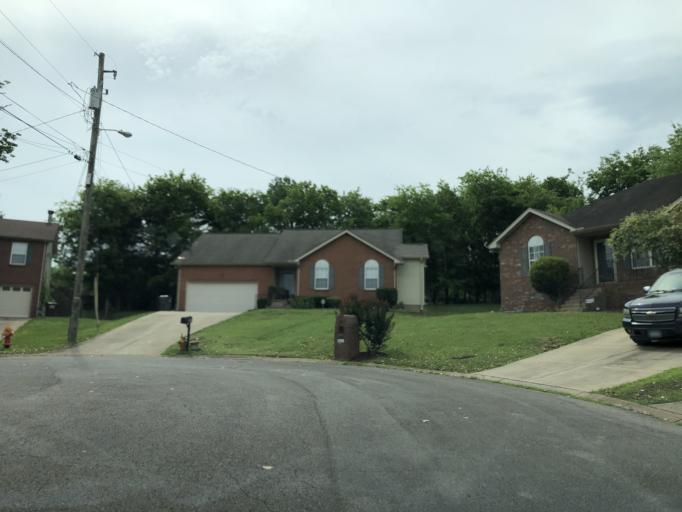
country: US
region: Tennessee
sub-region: Davidson County
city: Goodlettsville
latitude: 36.2835
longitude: -86.7102
